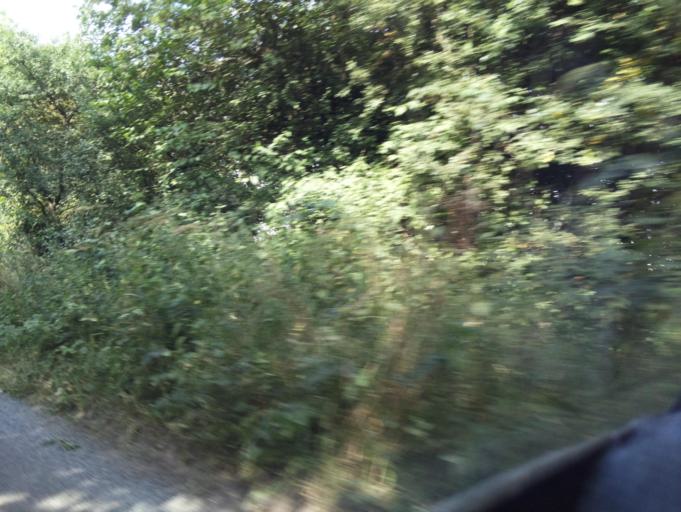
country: GB
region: England
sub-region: Wiltshire
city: Minety
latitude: 51.6456
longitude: -1.9759
